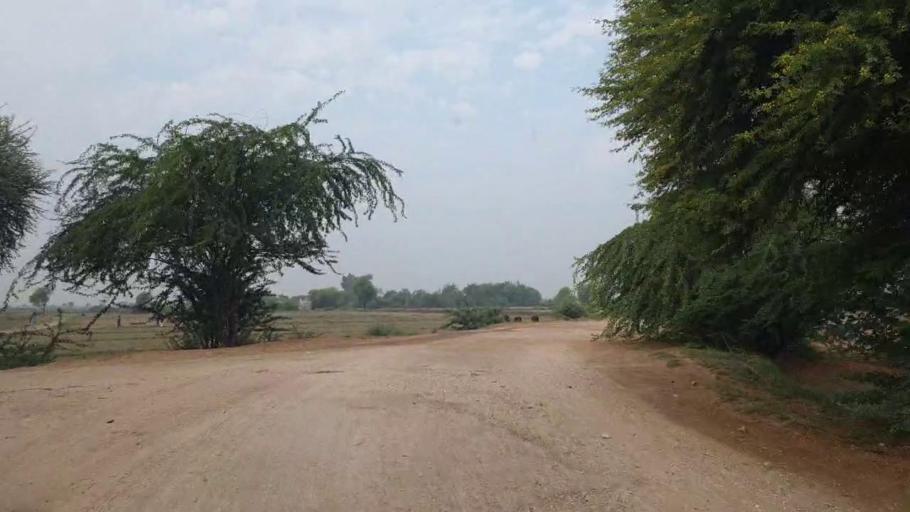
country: PK
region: Sindh
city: Tando Bago
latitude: 24.7897
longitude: 68.8805
